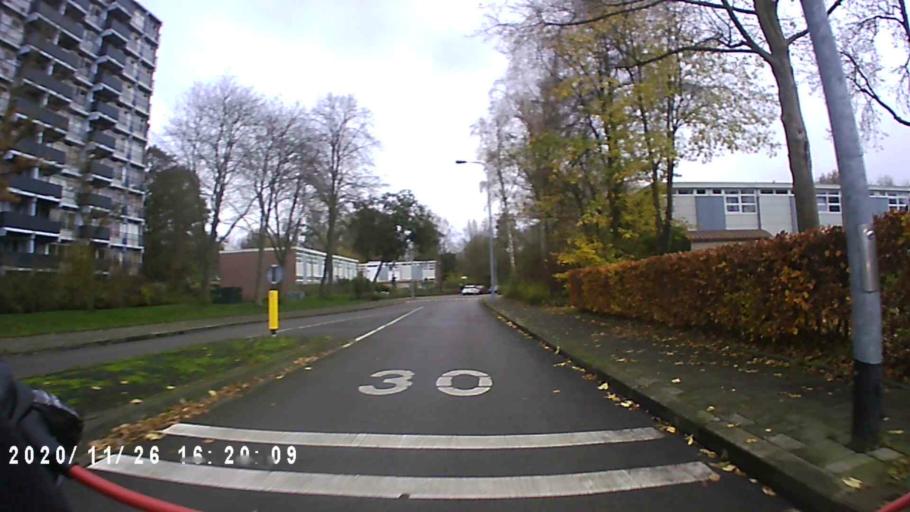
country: NL
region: Groningen
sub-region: Gemeente Groningen
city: Oosterpark
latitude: 53.2349
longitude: 6.6249
